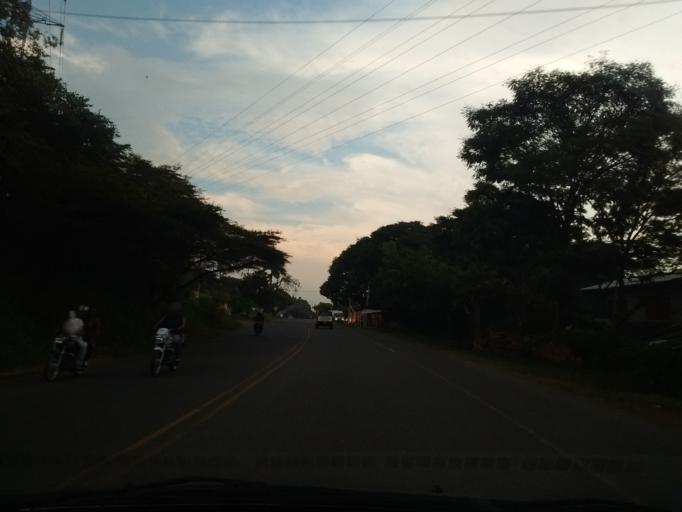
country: CO
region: Cauca
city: Santander de Quilichao
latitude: 2.9996
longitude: -76.4931
